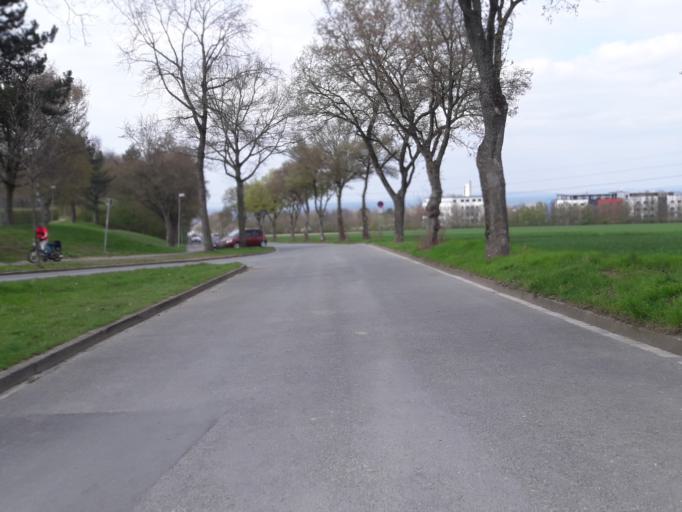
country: DE
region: North Rhine-Westphalia
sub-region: Regierungsbezirk Detmold
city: Paderborn
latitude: 51.6970
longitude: 8.7614
